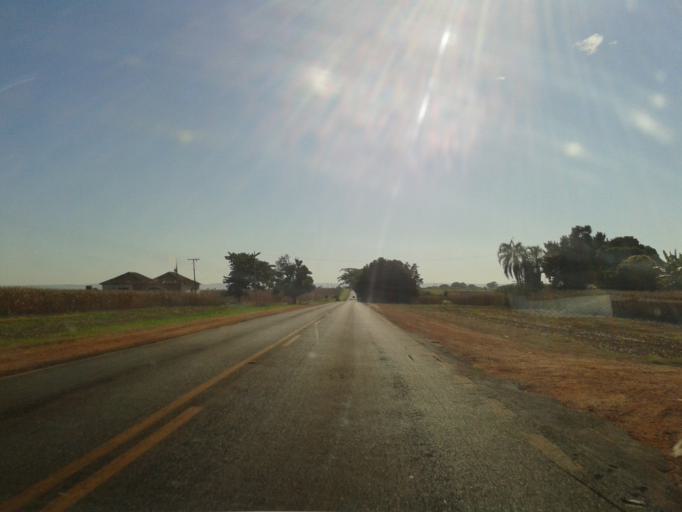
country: BR
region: Minas Gerais
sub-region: Capinopolis
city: Capinopolis
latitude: -18.5907
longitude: -49.5165
